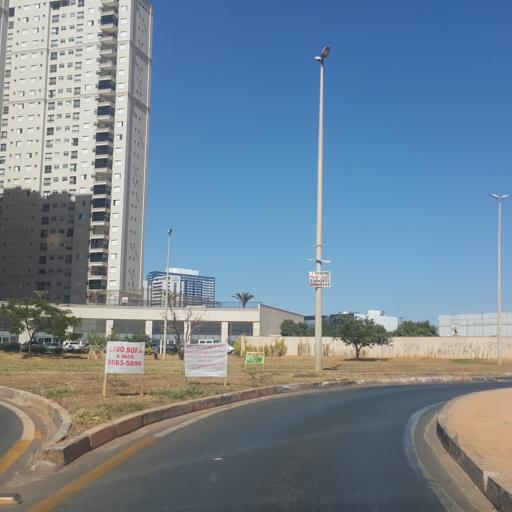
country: BR
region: Federal District
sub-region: Brasilia
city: Brasilia
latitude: -15.8333
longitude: -48.0439
